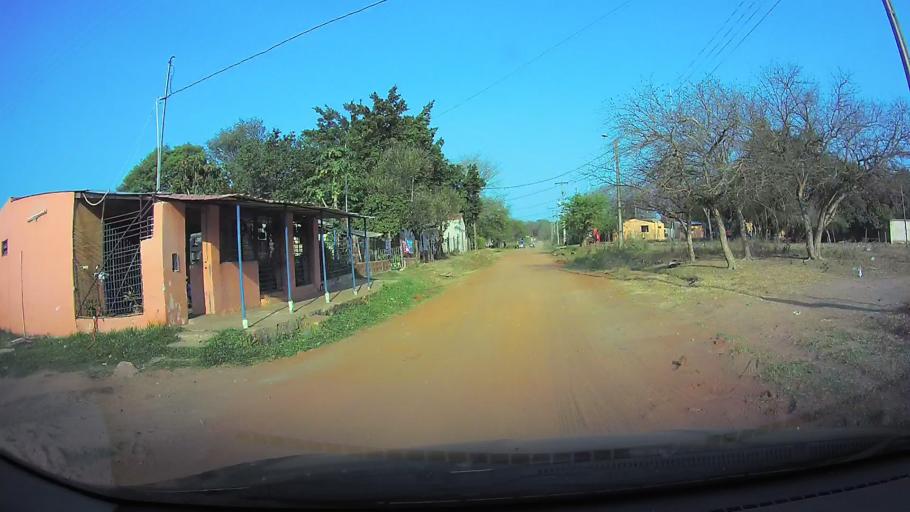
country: PY
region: Central
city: Limpio
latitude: -25.2189
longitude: -57.4881
